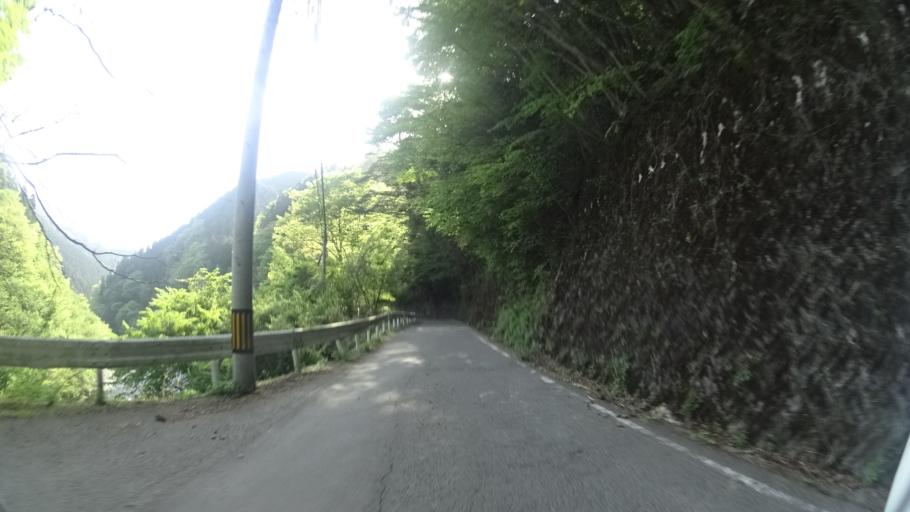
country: JP
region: Tokushima
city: Ikedacho
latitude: 33.8727
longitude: 133.9787
